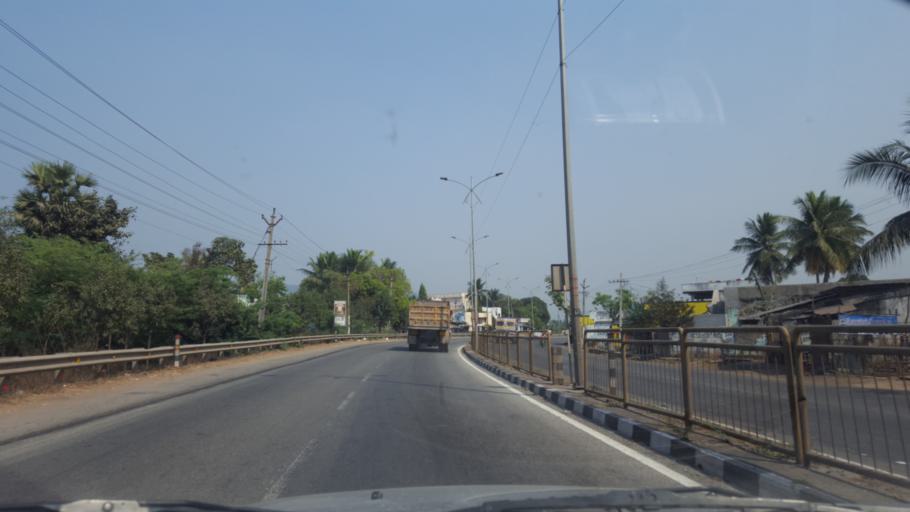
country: IN
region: Andhra Pradesh
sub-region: Vishakhapatnam
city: Anakapalle
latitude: 17.6894
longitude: 83.0733
